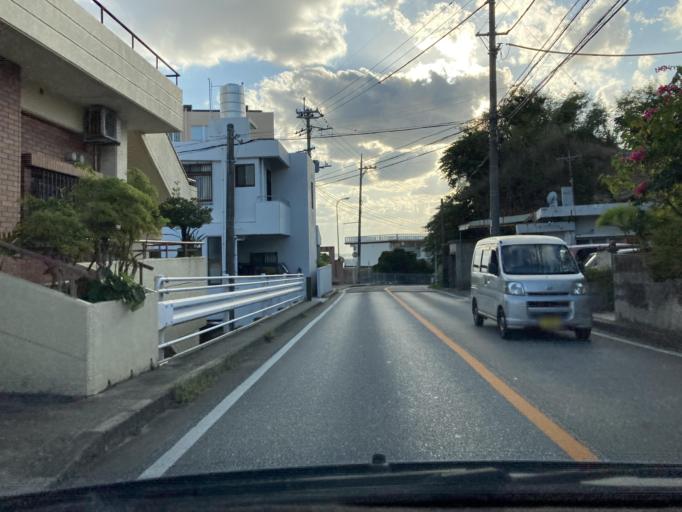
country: JP
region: Okinawa
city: Chatan
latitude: 26.3170
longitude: 127.7737
